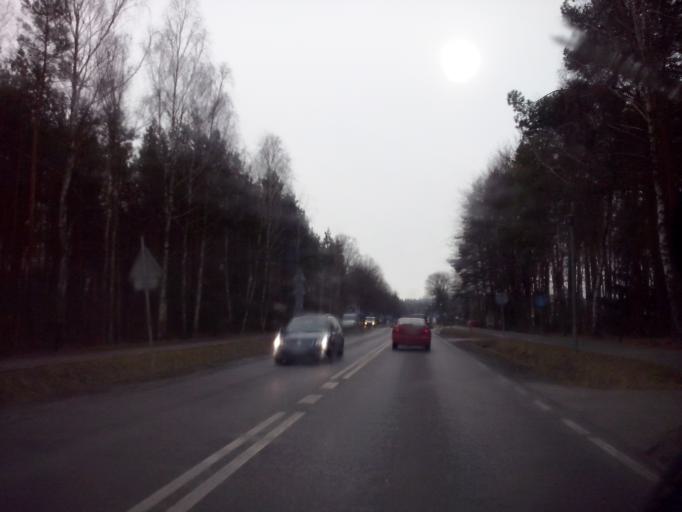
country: PL
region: Lublin Voivodeship
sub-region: Powiat zamojski
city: Zwierzyniec
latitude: 50.6176
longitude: 22.9672
